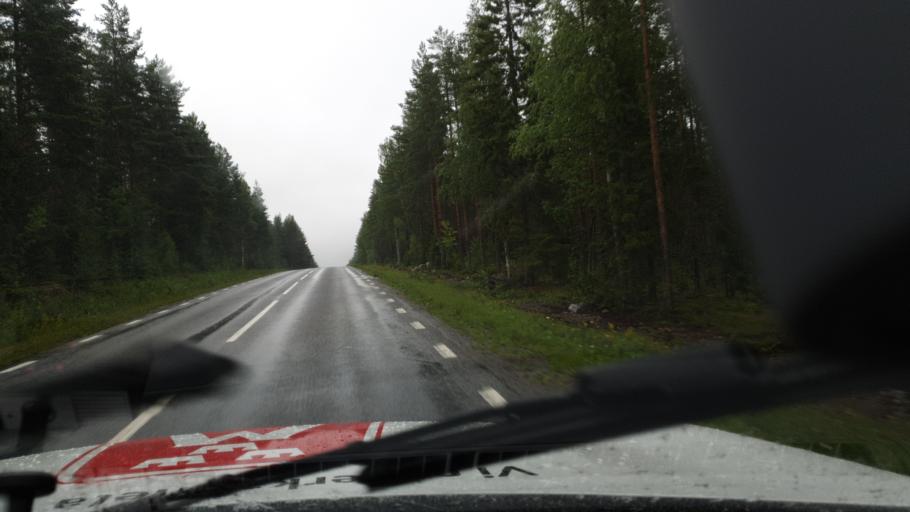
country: SE
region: Vaesterbotten
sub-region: Skelleftea Kommun
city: Viken
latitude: 64.6692
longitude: 20.8625
